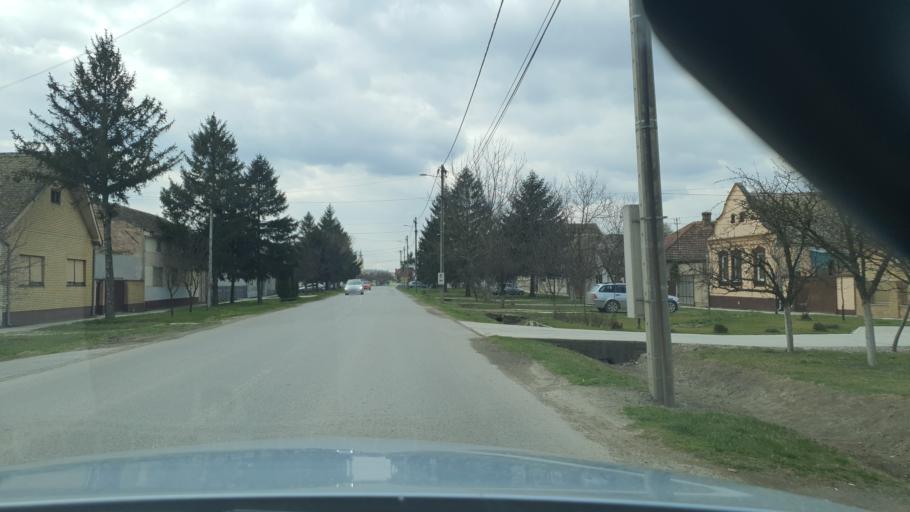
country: RS
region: Autonomna Pokrajina Vojvodina
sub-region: Juznobacki Okrug
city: Bac
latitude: 45.3958
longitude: 19.2399
